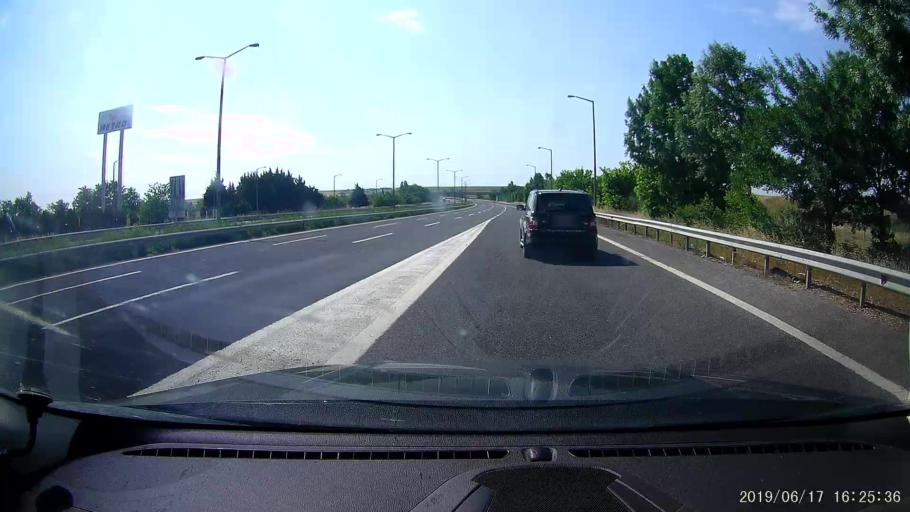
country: TR
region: Tekirdag
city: Marmaracik
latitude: 41.2928
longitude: 27.7788
